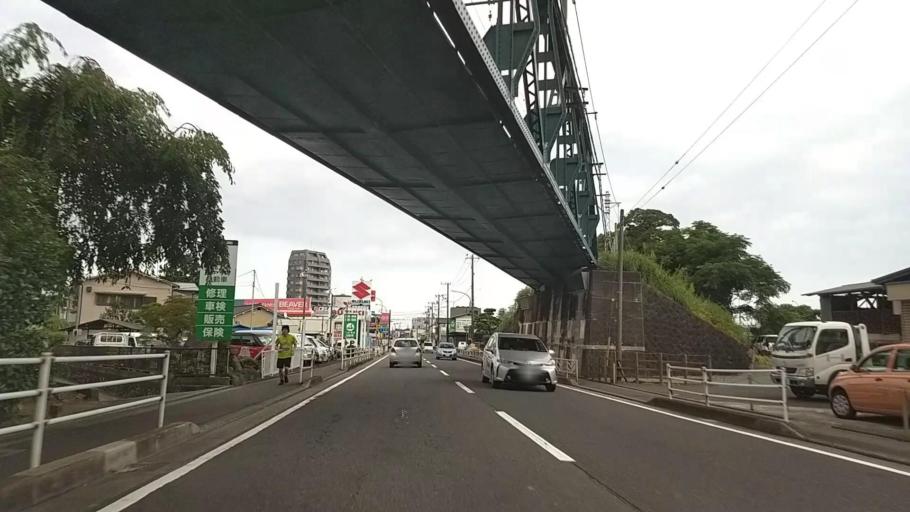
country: JP
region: Kanagawa
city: Odawara
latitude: 35.2467
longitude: 139.1408
